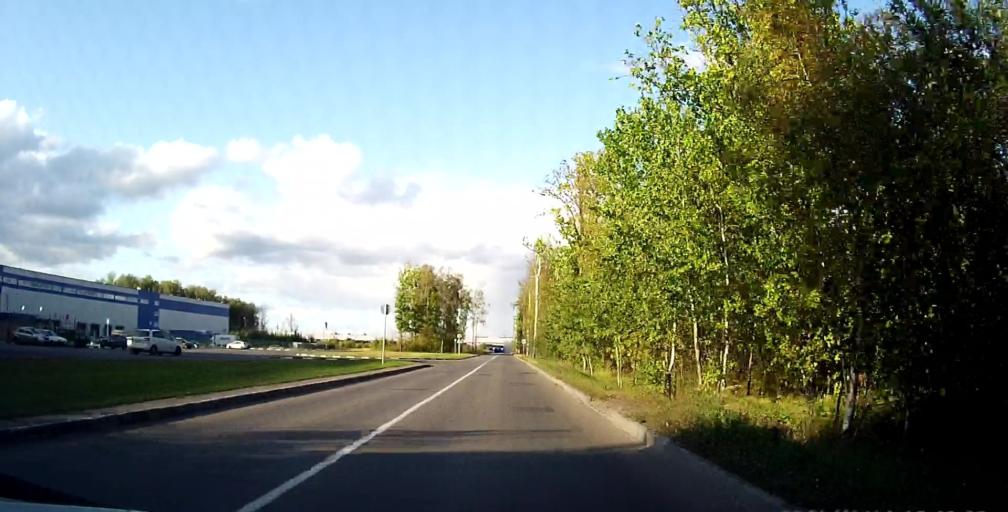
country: RU
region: Moskovskaya
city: Klimovsk
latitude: 55.3632
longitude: 37.5656
